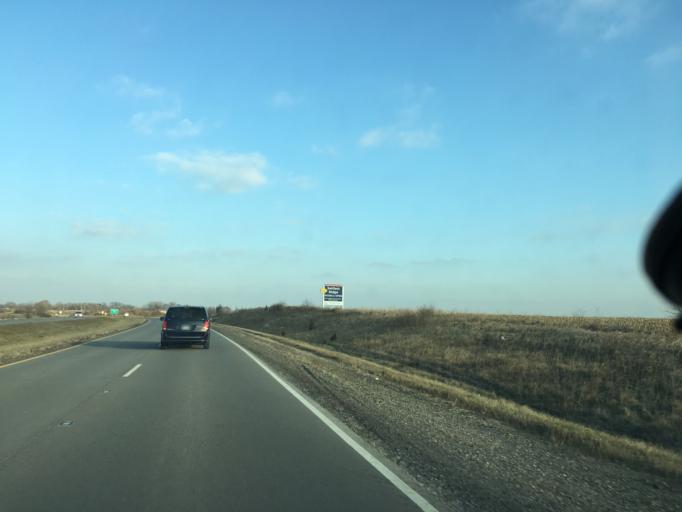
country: US
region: Illinois
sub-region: Kane County
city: Sugar Grove
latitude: 41.7655
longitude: -88.4256
